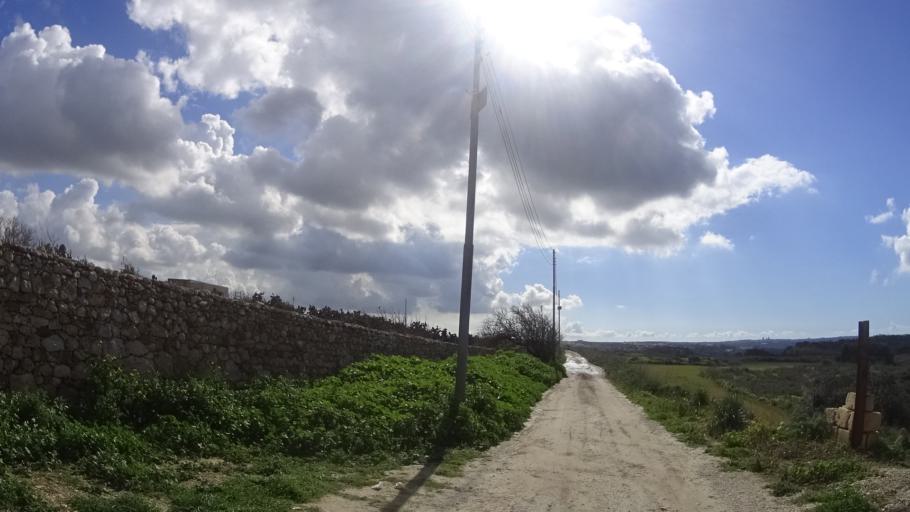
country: MT
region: L-Imtarfa
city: Imtarfa
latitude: 35.9046
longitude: 14.3844
